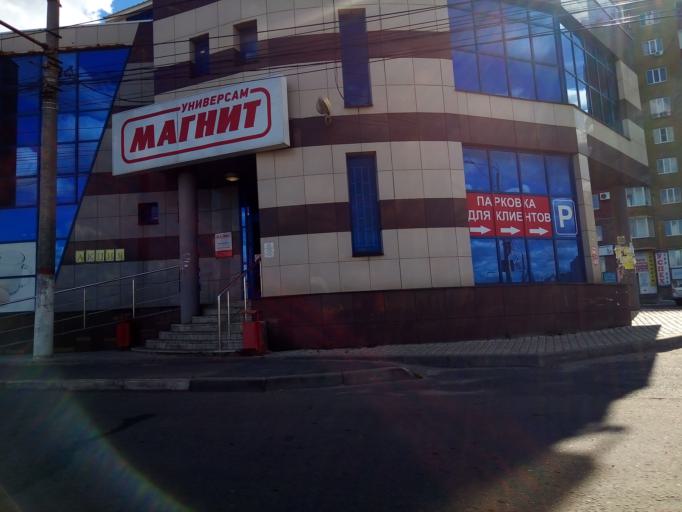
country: RU
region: Kursk
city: Kursk
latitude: 51.7740
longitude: 36.1781
